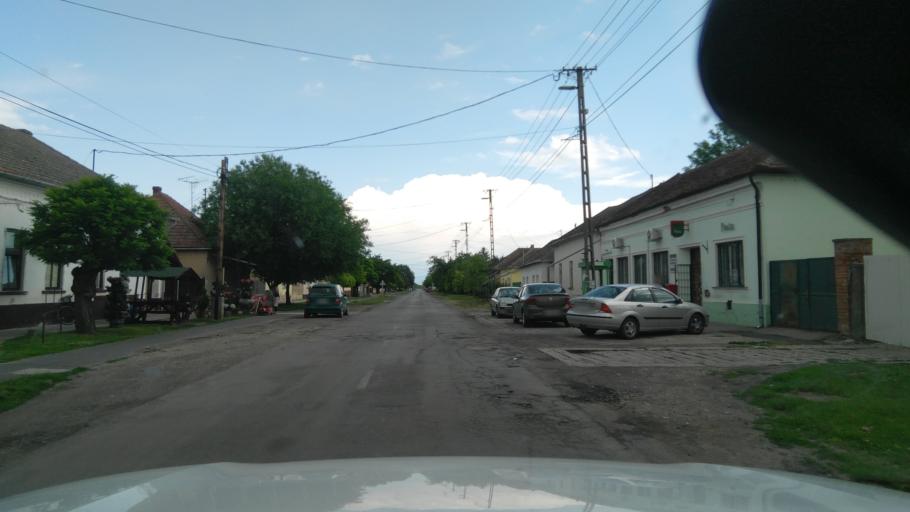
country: HU
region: Bekes
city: Magyarbanhegyes
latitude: 46.4560
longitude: 20.9656
